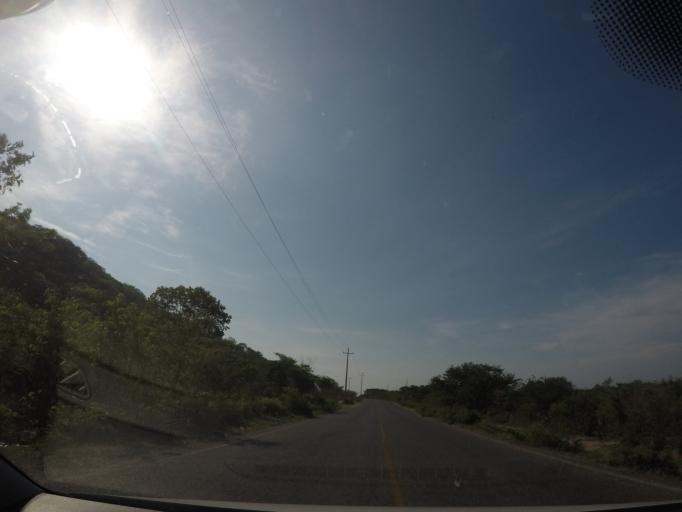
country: MX
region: Oaxaca
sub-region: Salina Cruz
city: Salina Cruz
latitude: 16.2297
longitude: -95.1413
